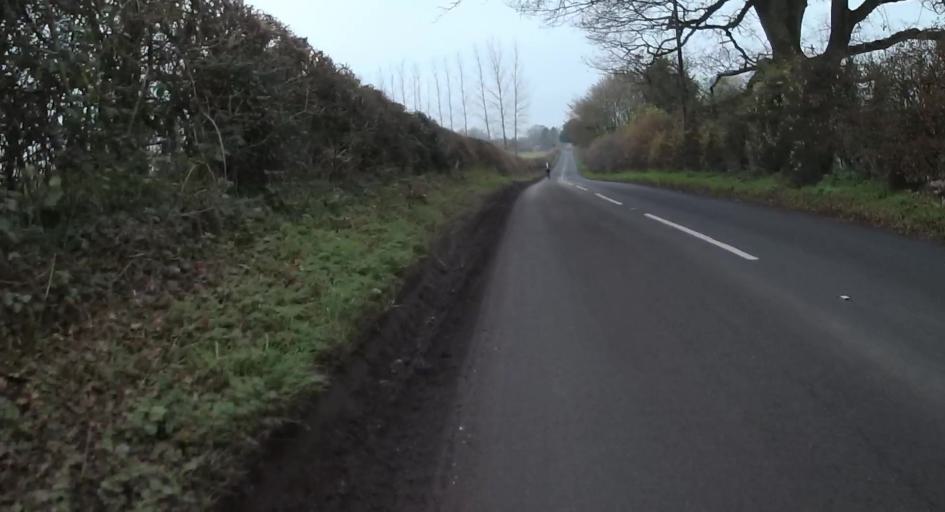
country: GB
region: England
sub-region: Hampshire
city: Kings Worthy
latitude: 51.1413
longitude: -1.1830
